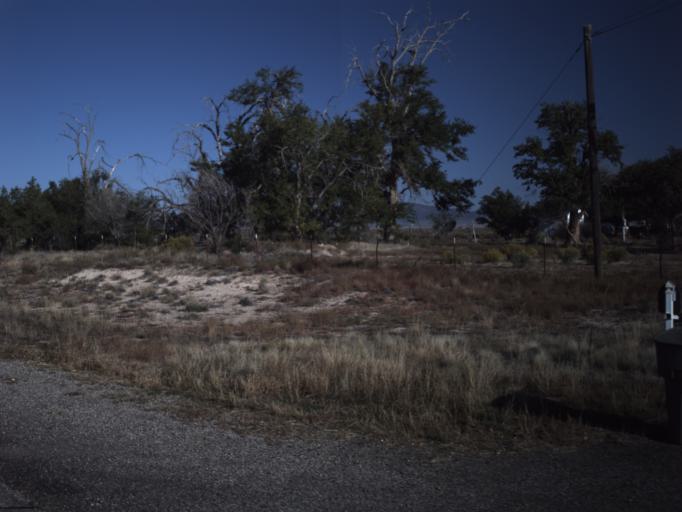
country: US
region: Utah
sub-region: Washington County
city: Enterprise
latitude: 37.7246
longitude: -113.6982
